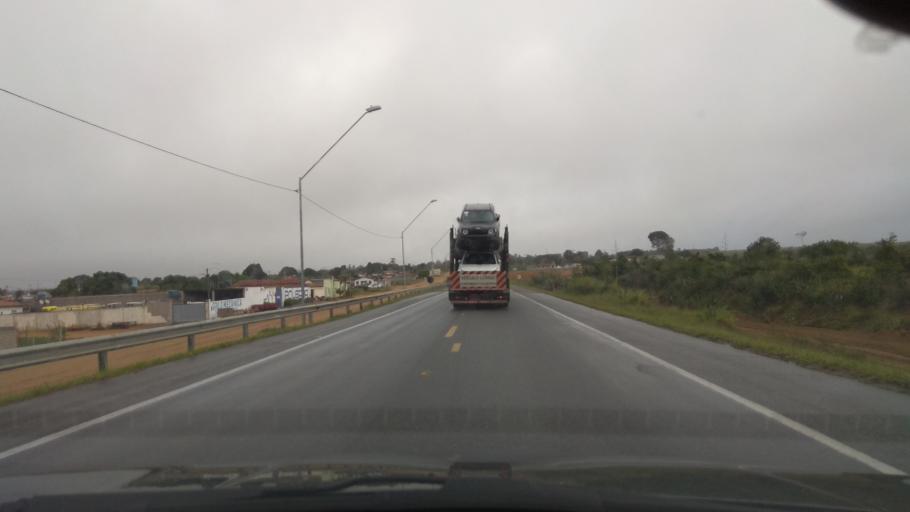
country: BR
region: Bahia
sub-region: Santa Ines
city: Santa Ines
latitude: -13.0790
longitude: -39.9619
